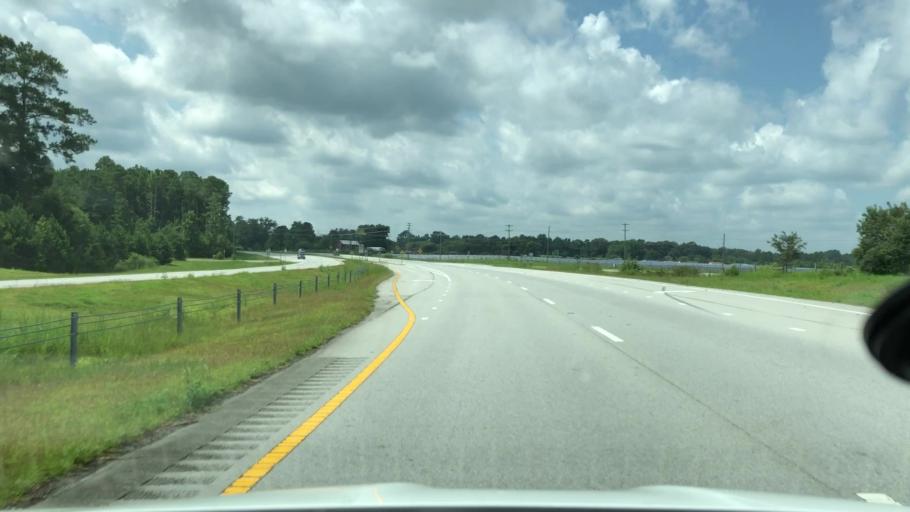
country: US
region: North Carolina
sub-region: Beaufort County
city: Washington
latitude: 35.5018
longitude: -77.1017
